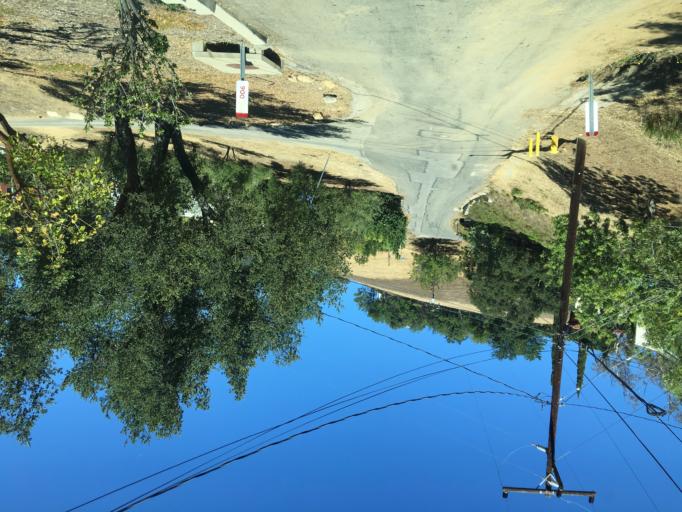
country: US
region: California
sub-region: Los Angeles County
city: Malibu Beach
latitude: 34.0614
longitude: -118.7439
